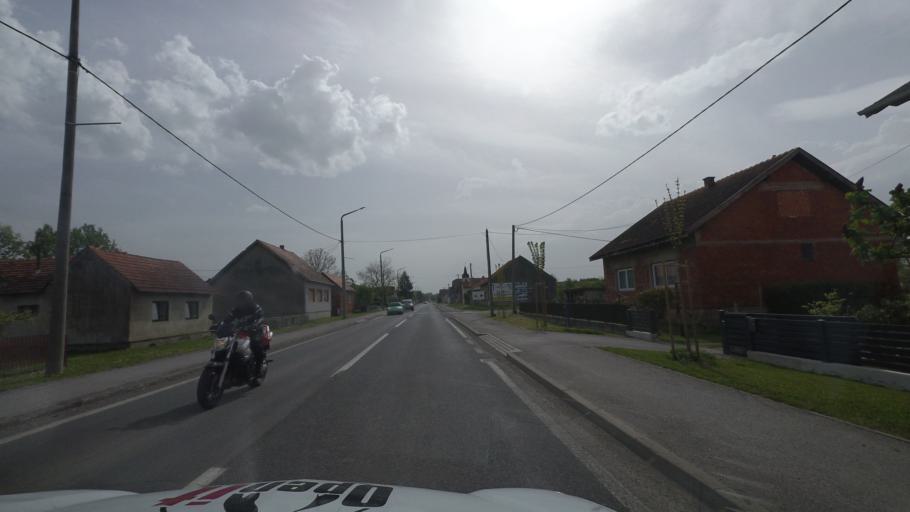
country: HR
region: Sisacko-Moslavacka
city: Glina
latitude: 45.3508
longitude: 16.0989
